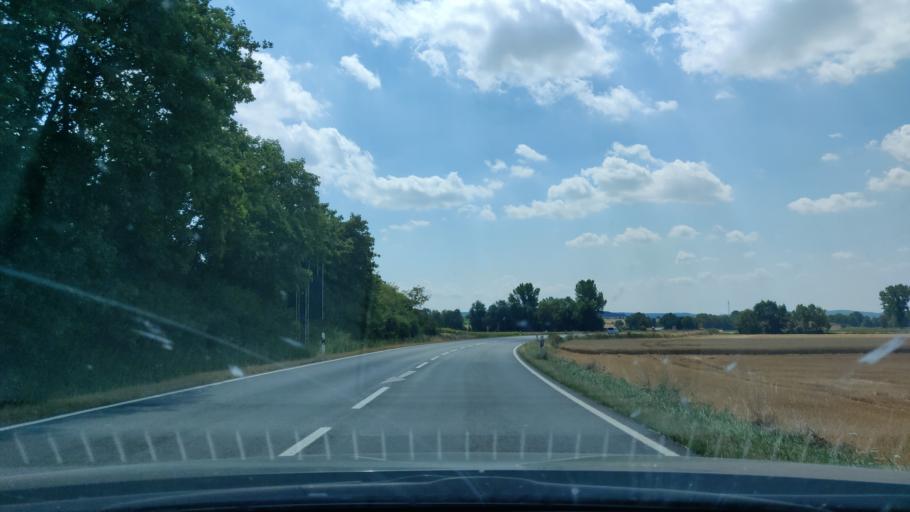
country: DE
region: Hesse
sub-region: Regierungsbezirk Kassel
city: Homberg
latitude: 51.0575
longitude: 9.3868
